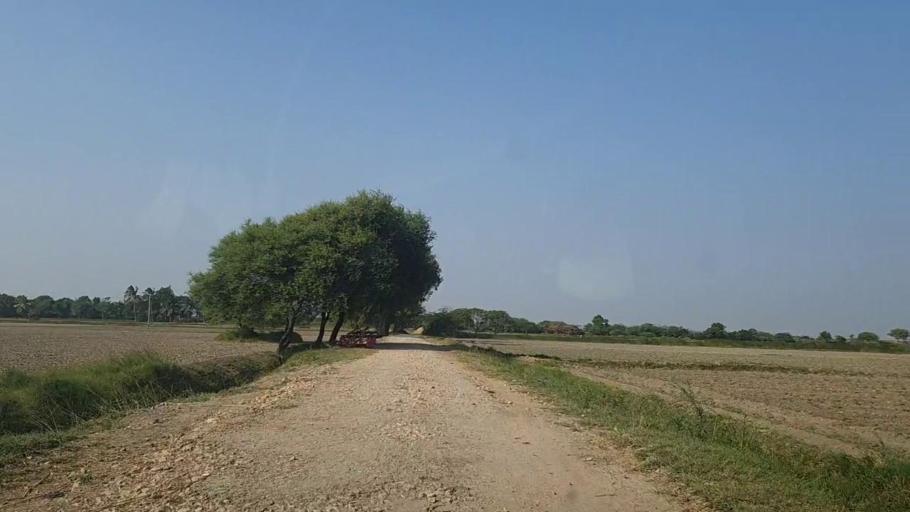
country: PK
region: Sindh
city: Mirpur Sakro
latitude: 24.5713
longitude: 67.6847
